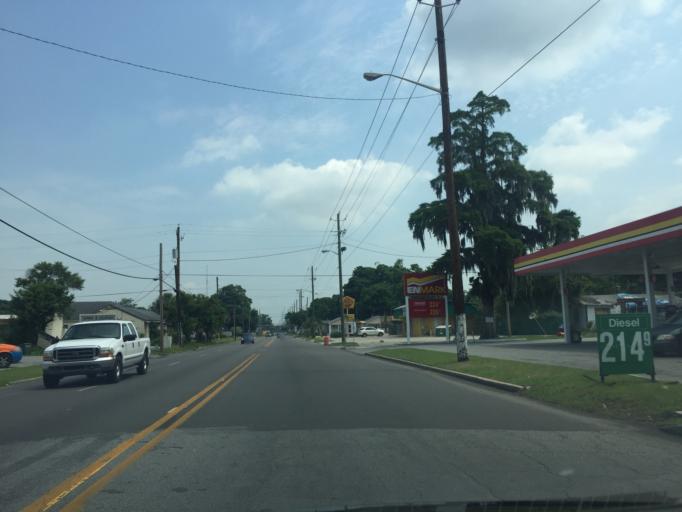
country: US
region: Georgia
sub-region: Chatham County
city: Savannah
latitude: 32.0415
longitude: -81.1107
